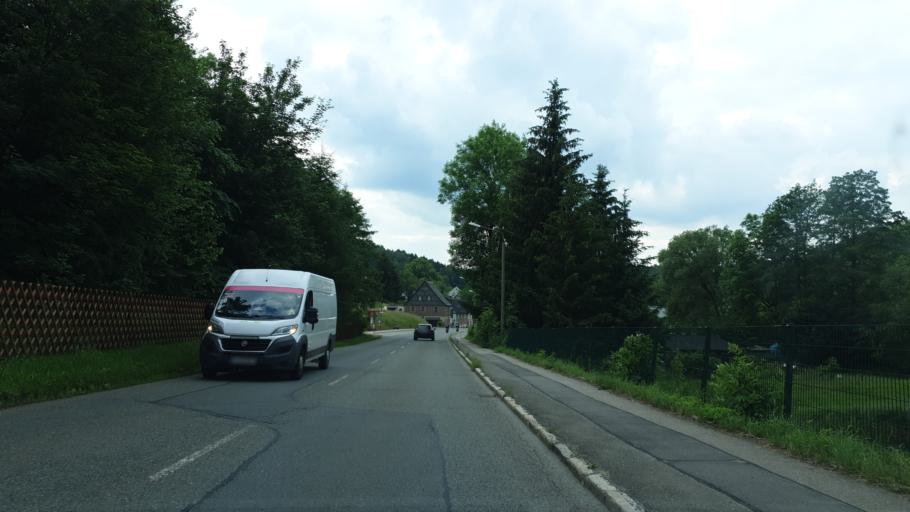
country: DE
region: Saxony
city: Aue
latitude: 50.6114
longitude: 12.7079
